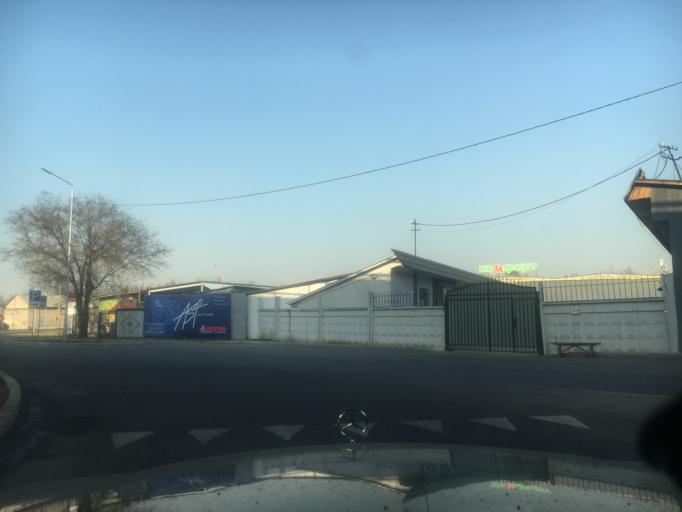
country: KZ
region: Almaty Qalasy
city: Almaty
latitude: 43.2748
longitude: 76.9453
